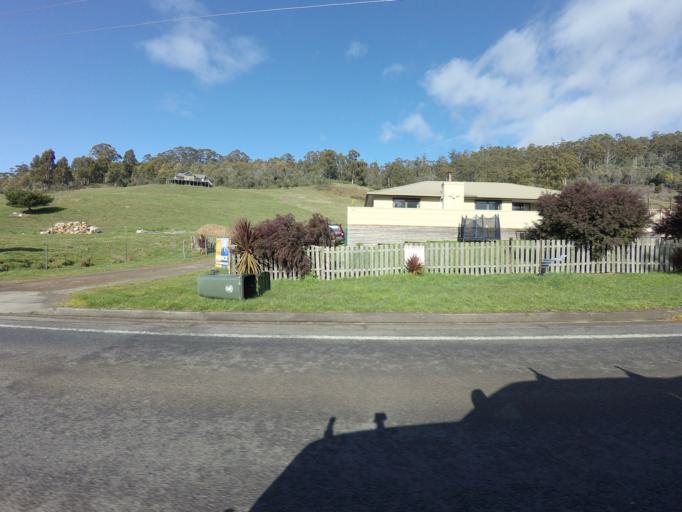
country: AU
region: Tasmania
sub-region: Huon Valley
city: Geeveston
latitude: -43.3040
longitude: 147.0076
